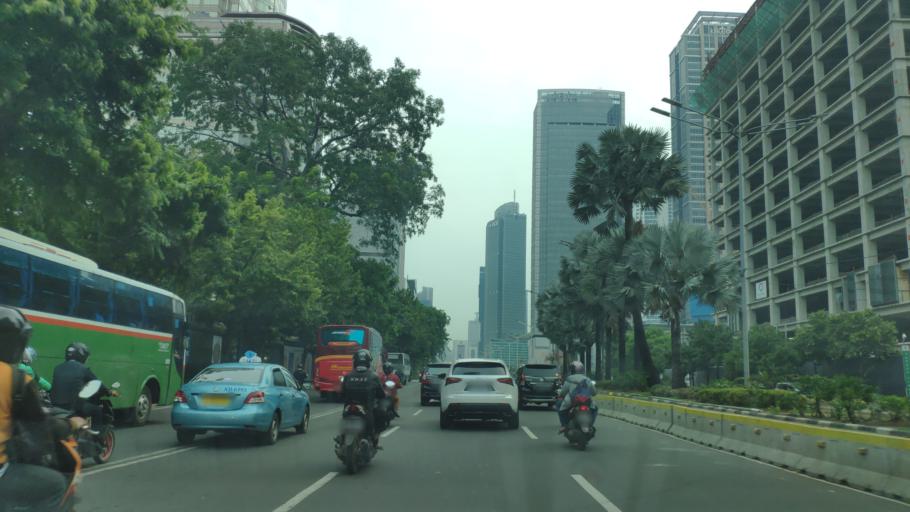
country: ID
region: Jakarta Raya
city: Jakarta
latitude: -6.1885
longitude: 106.8231
